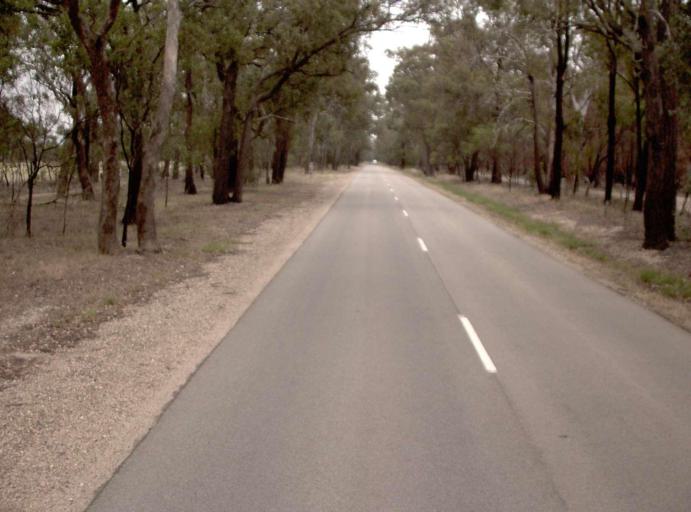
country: AU
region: Victoria
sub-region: Wellington
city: Heyfield
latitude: -37.9604
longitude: 146.7736
